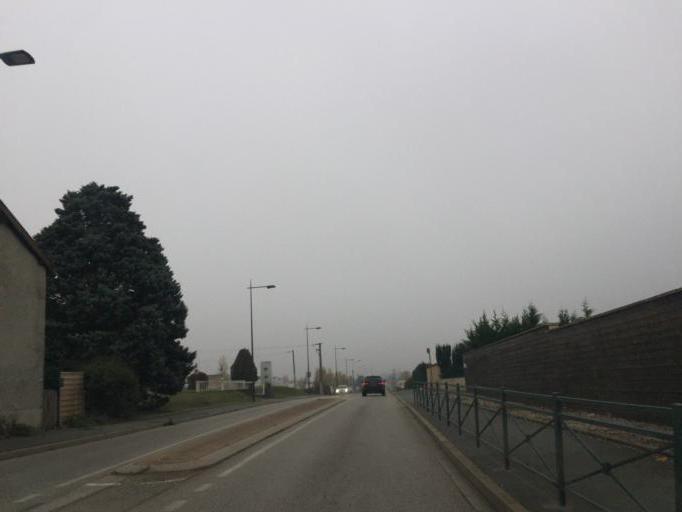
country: FR
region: Rhone-Alpes
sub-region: Departement de l'Ain
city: Mionnay
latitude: 45.8689
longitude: 4.9132
